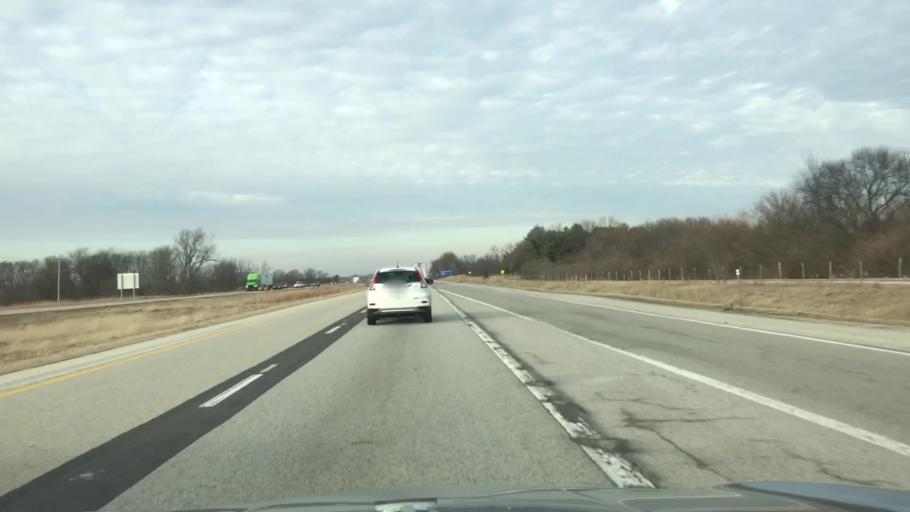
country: US
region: Illinois
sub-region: Sangamon County
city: Divernon
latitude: 39.5717
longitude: -89.6461
